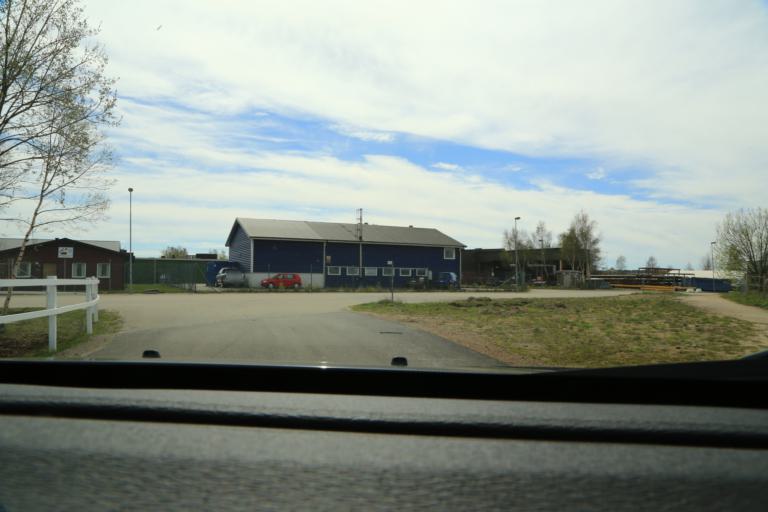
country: SE
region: Halland
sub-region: Varbergs Kommun
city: Varberg
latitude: 57.1285
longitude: 12.2887
